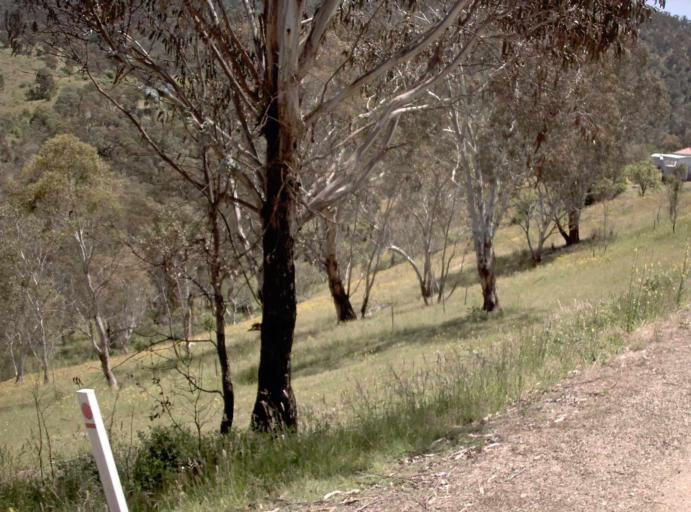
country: AU
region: Victoria
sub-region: Alpine
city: Mount Beauty
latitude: -37.1064
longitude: 147.5811
